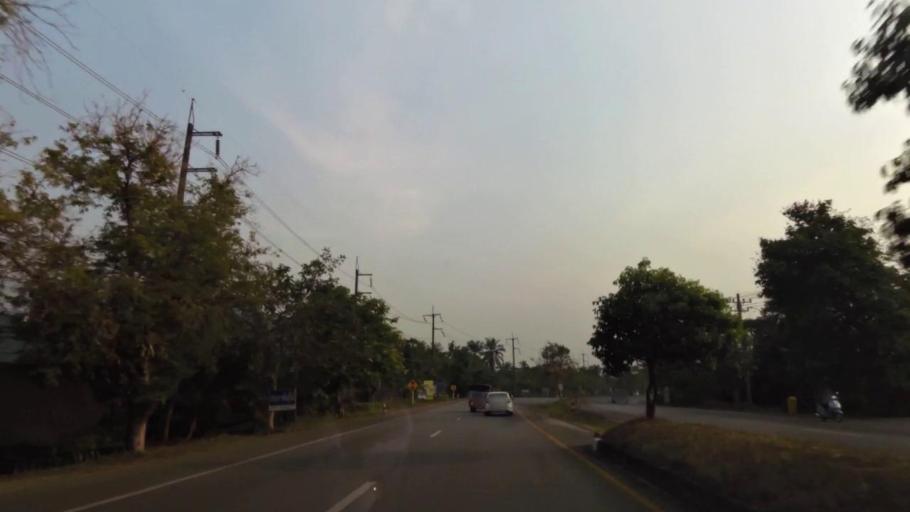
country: TH
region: Chanthaburi
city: Khlung
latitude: 12.5135
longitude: 102.1686
